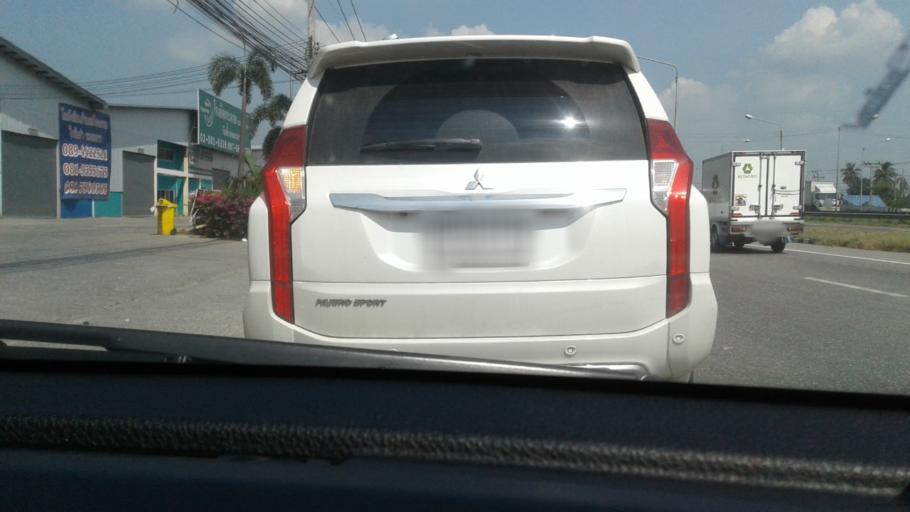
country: TH
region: Nonthaburi
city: Bang Bua Thong
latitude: 13.9509
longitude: 100.4233
